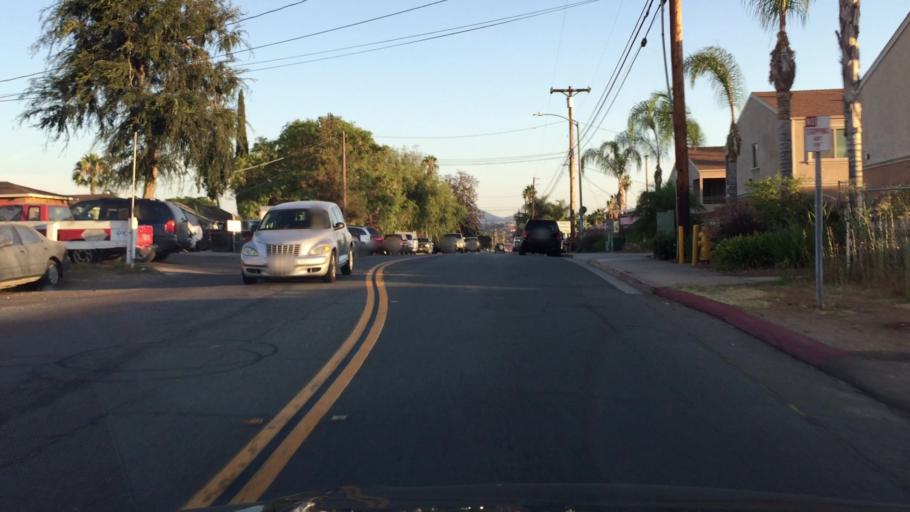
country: US
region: California
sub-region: San Diego County
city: Bostonia
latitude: 32.8130
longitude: -116.9447
